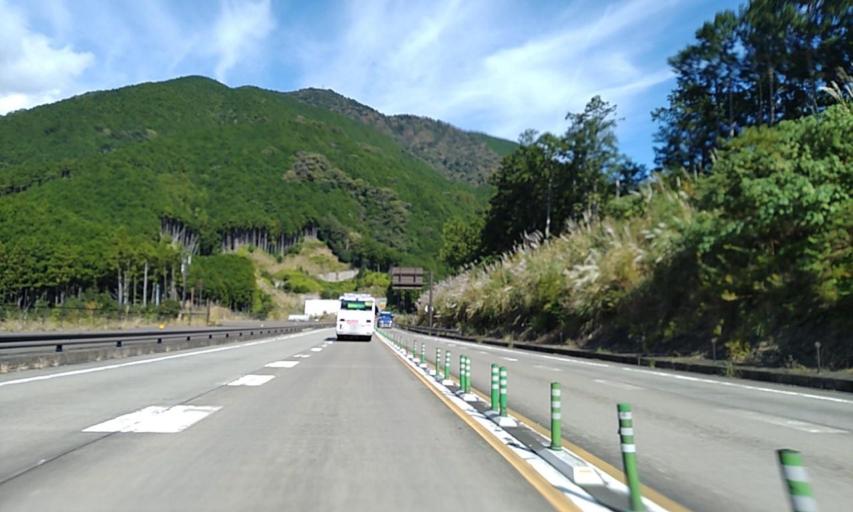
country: JP
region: Mie
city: Owase
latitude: 33.9731
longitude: 136.1646
